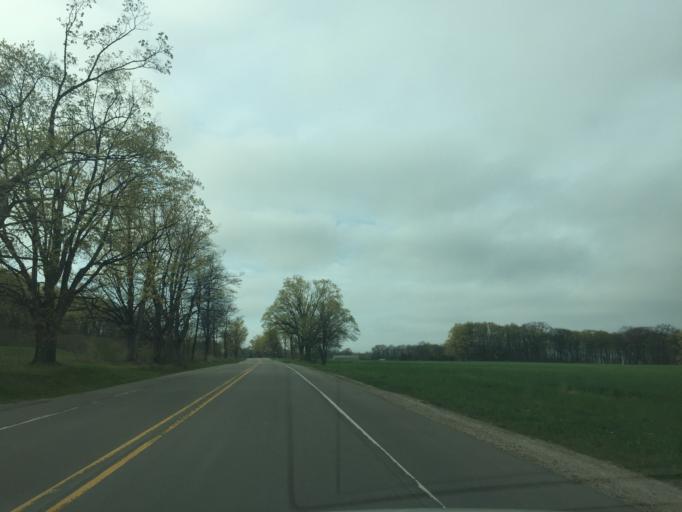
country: US
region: Michigan
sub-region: Leelanau County
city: Leland
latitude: 45.0703
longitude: -85.5874
